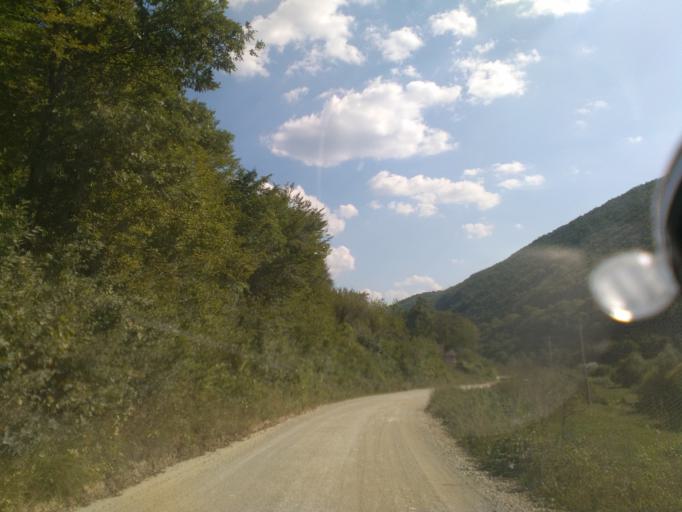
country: BA
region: Federation of Bosnia and Herzegovina
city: Orasac
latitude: 44.5111
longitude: 16.1277
